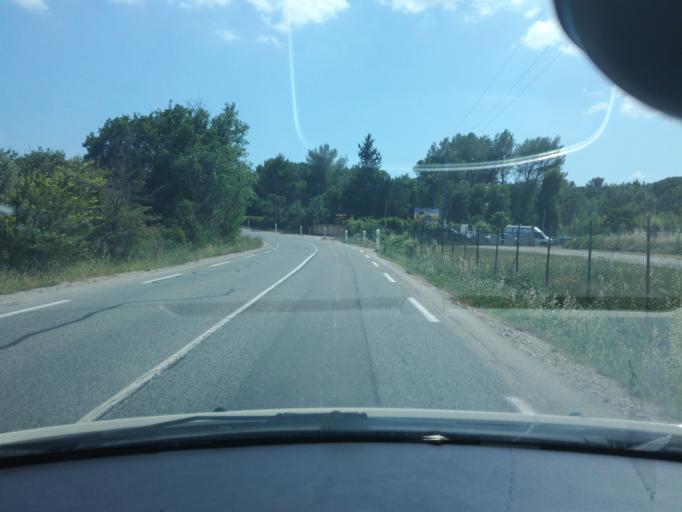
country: FR
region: Provence-Alpes-Cote d'Azur
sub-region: Departement du Var
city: Le Muy
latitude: 43.4893
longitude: 6.5651
